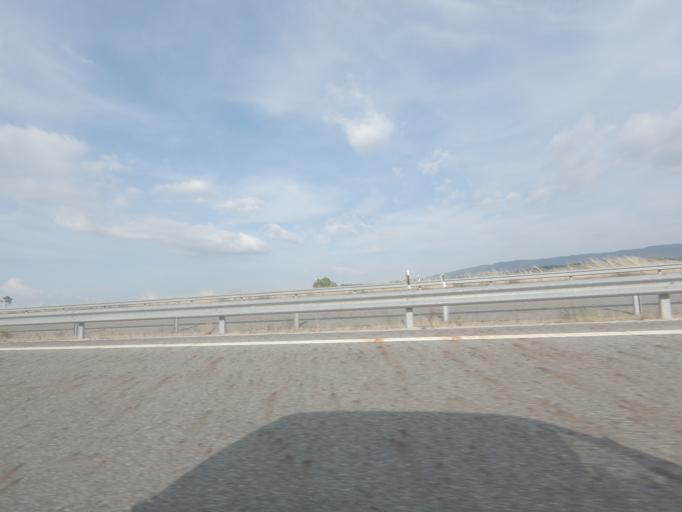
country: PT
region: Vila Real
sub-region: Chaves
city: Chaves
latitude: 41.7388
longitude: -7.5258
